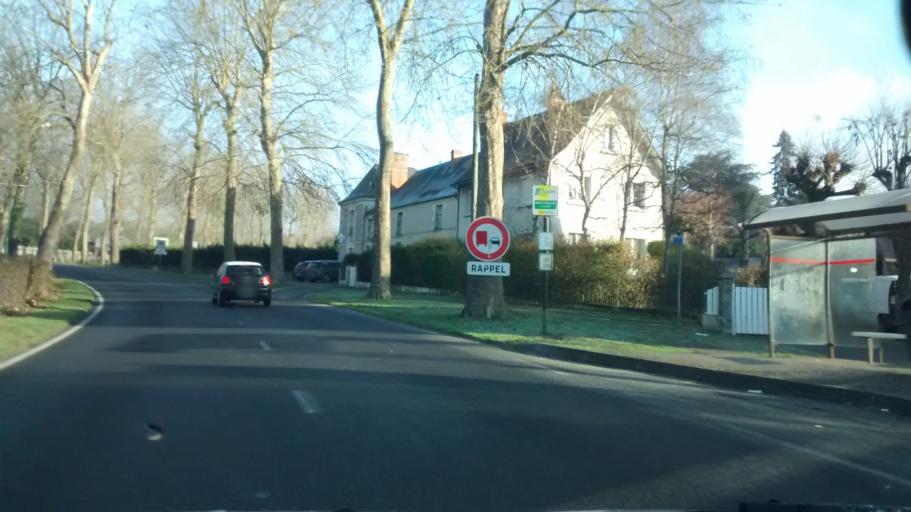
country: FR
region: Centre
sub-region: Departement d'Indre-et-Loire
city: Montbazon
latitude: 47.2901
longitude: 0.7186
